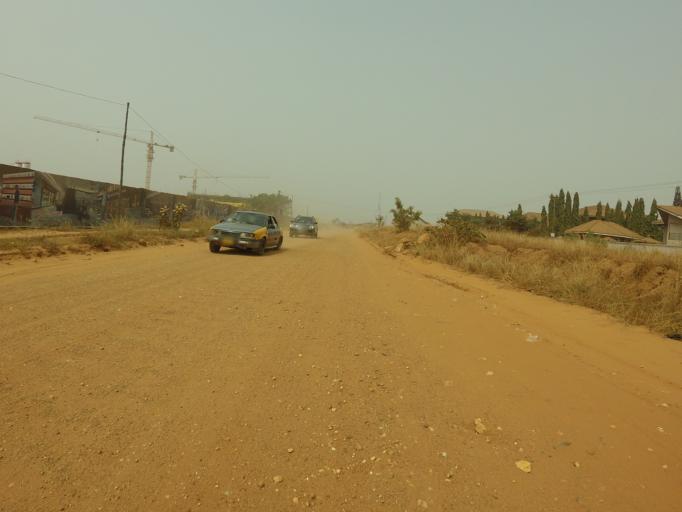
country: GH
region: Greater Accra
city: Medina Estates
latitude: 5.6328
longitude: -0.1247
